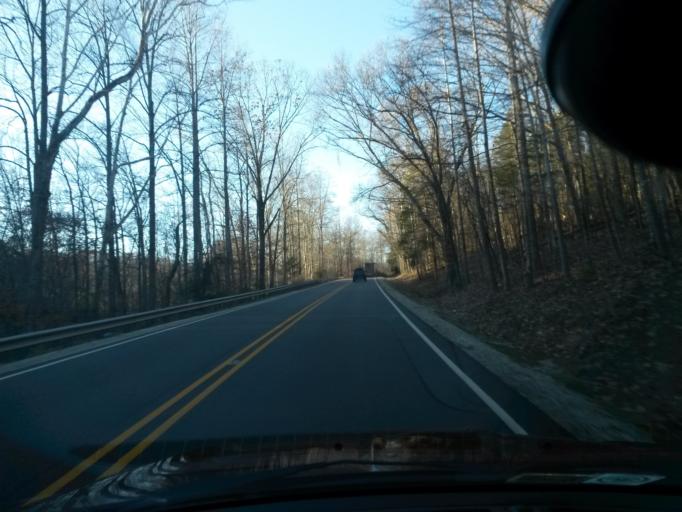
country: US
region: Virginia
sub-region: Amherst County
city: Amherst
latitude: 37.6145
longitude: -79.0889
